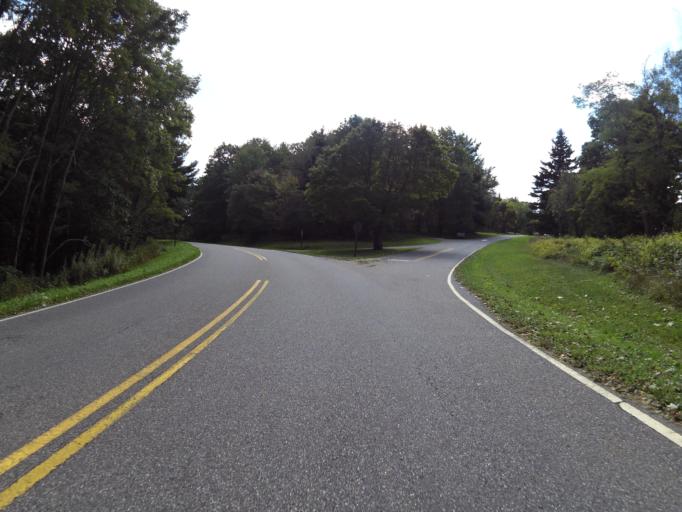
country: US
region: Virginia
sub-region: Page County
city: Luray
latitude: 38.6256
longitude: -78.3409
